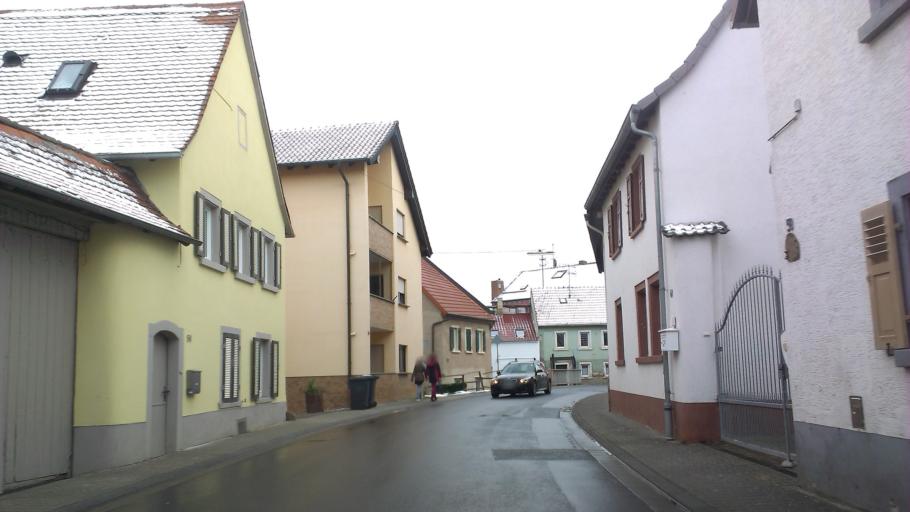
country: DE
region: Rheinland-Pfalz
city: Monsheim
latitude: 49.6361
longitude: 8.2094
